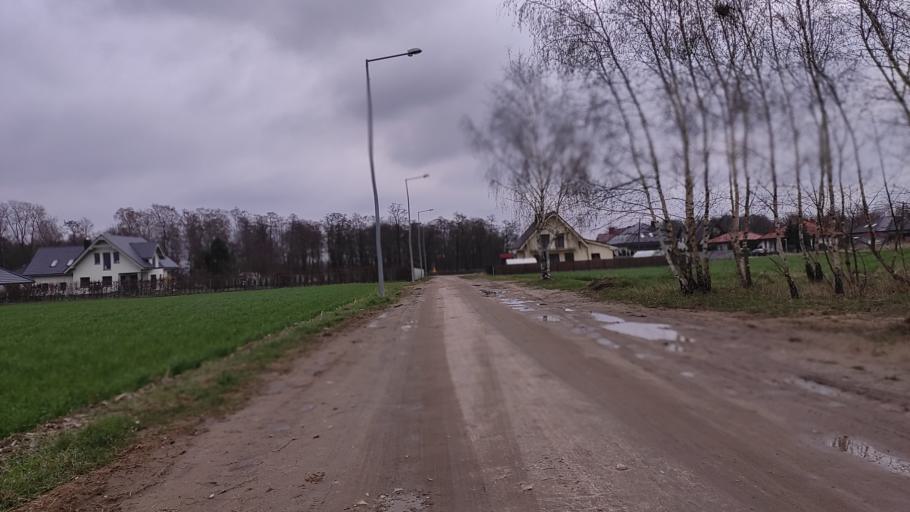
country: PL
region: Greater Poland Voivodeship
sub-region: Powiat poznanski
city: Kostrzyn
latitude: 52.4029
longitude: 17.1709
